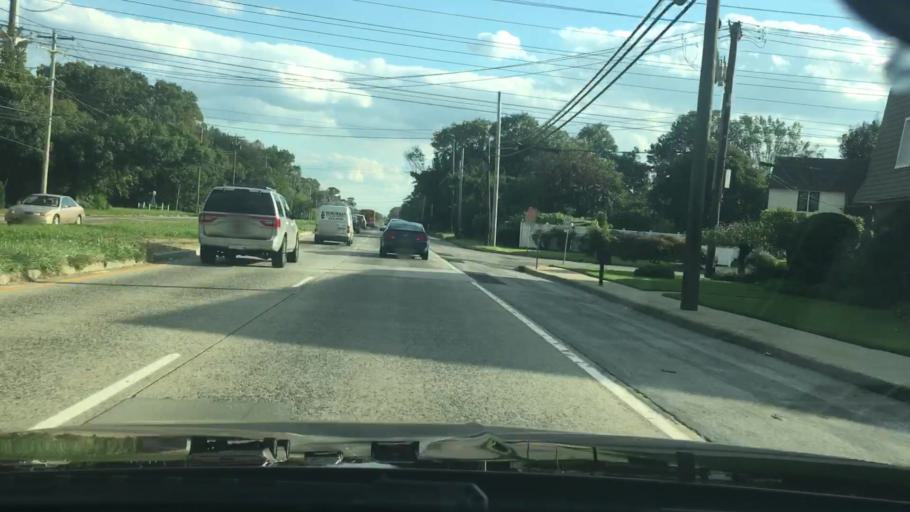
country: US
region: New York
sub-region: Suffolk County
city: Deer Park
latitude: 40.7797
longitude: -73.3373
